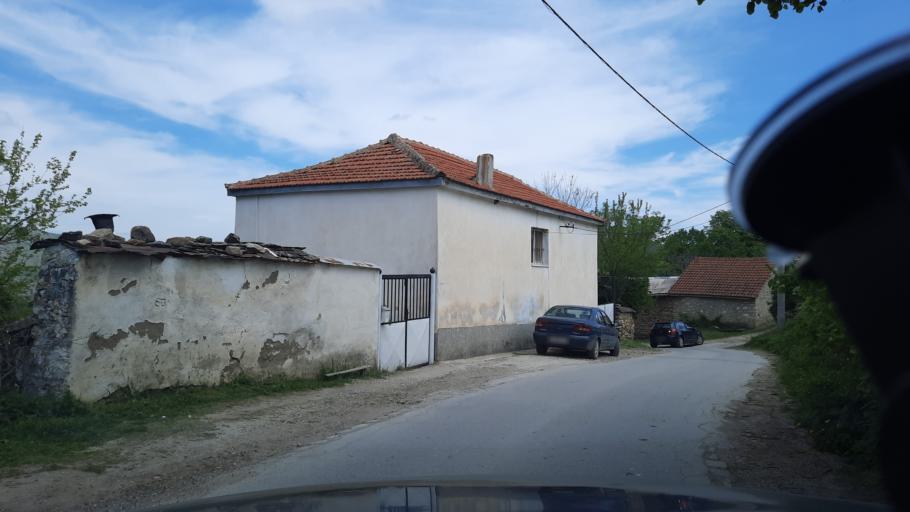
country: MK
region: Bitola
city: Bitola
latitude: 41.0246
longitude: 21.2846
